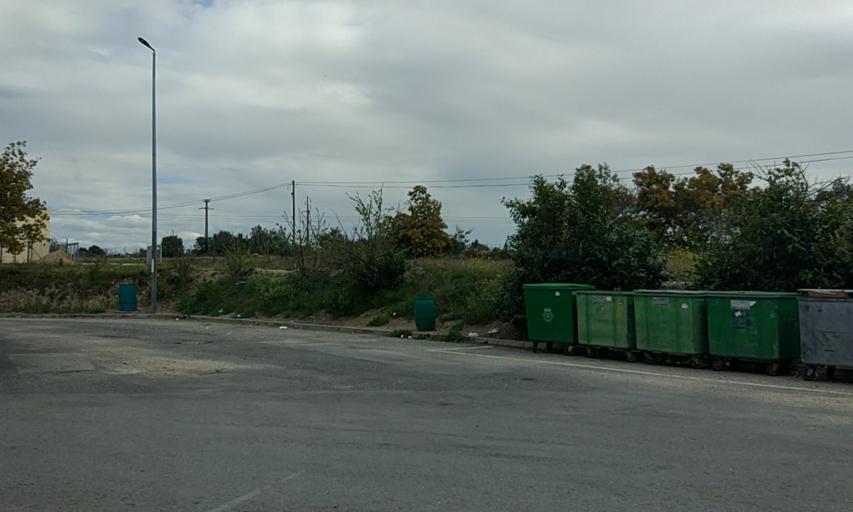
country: ES
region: Castille and Leon
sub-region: Provincia de Salamanca
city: Fuentes de Onoro
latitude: 40.6034
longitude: -6.9536
